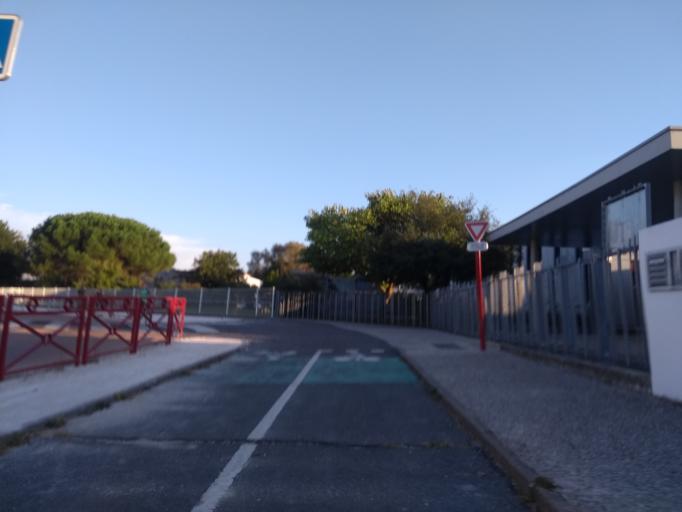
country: FR
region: Aquitaine
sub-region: Departement de la Gironde
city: Pessac
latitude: 44.7994
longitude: -0.6225
